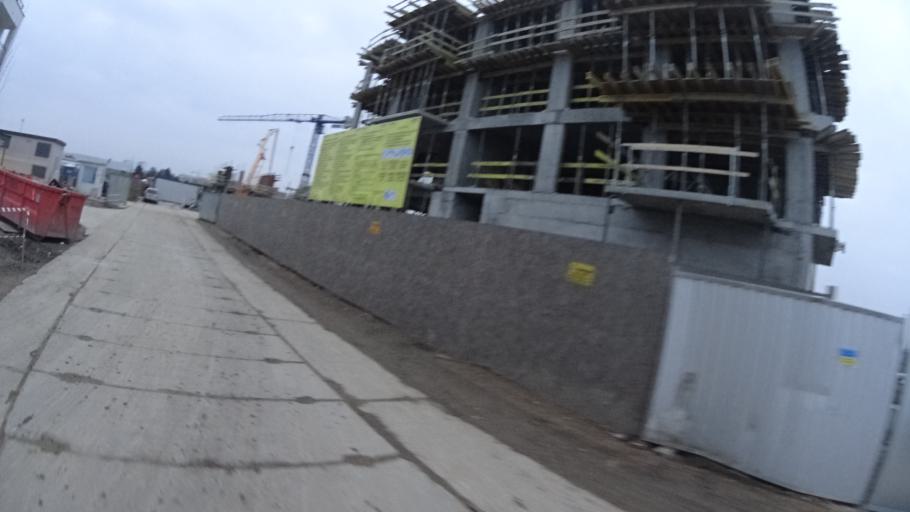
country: PL
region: Masovian Voivodeship
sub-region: Warszawa
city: Ursus
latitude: 52.2264
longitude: 20.8853
